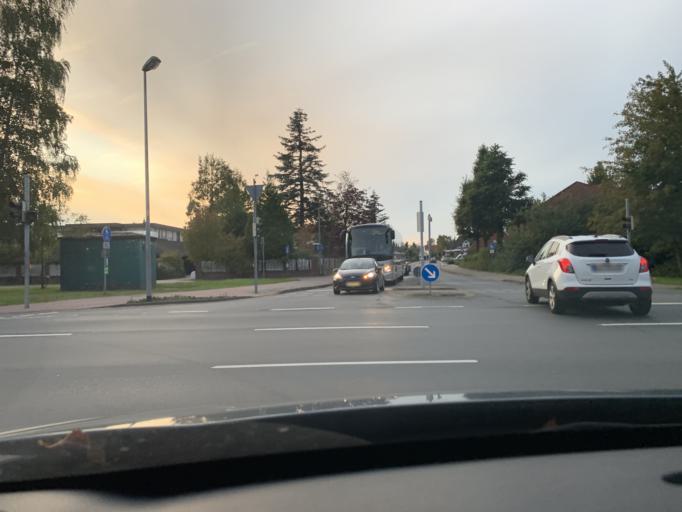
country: DE
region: Lower Saxony
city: Westerstede
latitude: 53.2571
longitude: 7.9351
